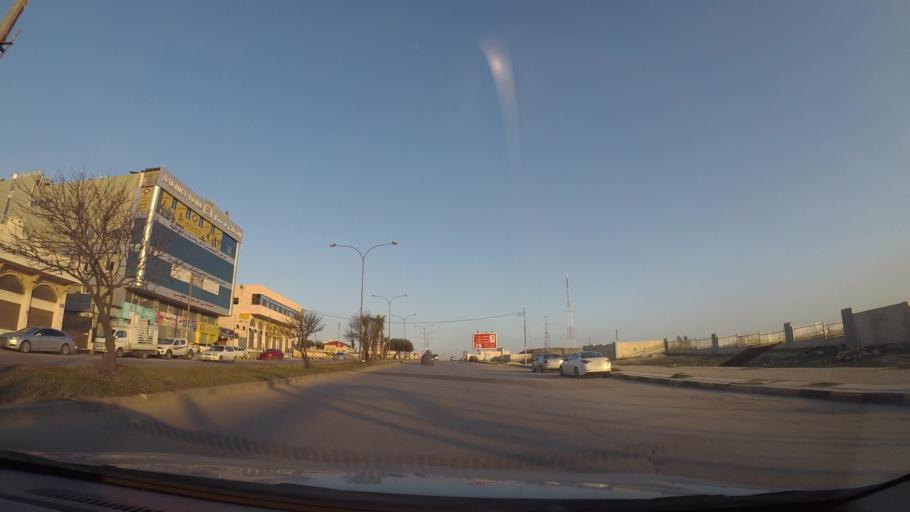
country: JO
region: Amman
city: Al Quwaysimah
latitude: 31.9093
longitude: 35.9272
